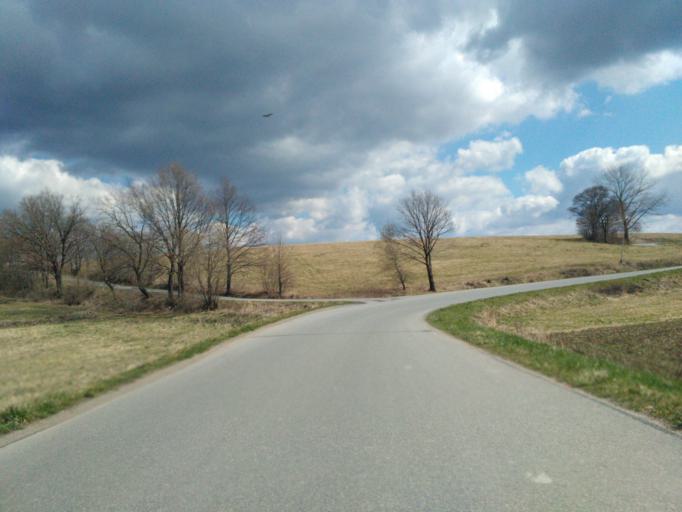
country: PL
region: Subcarpathian Voivodeship
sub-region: Powiat brzozowski
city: Dydnia
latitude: 49.6542
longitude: 22.2058
